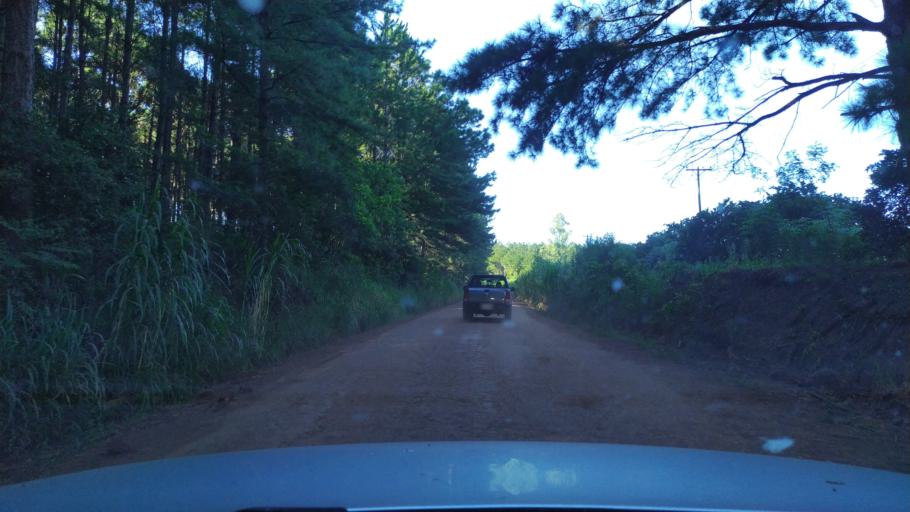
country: AR
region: Misiones
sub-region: Departamento de Montecarlo
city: Montecarlo
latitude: -26.6097
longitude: -54.6985
